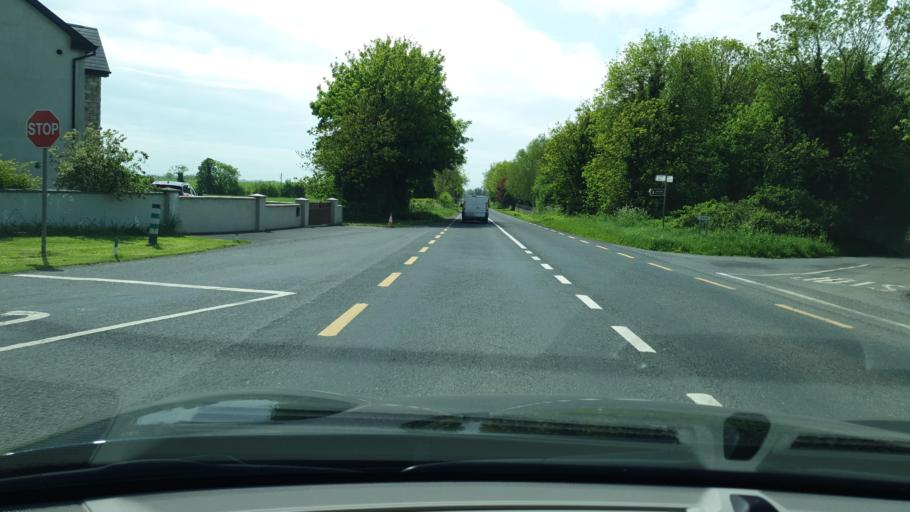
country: IE
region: Leinster
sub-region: An Mhi
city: Navan
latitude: 53.7692
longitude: -6.7254
